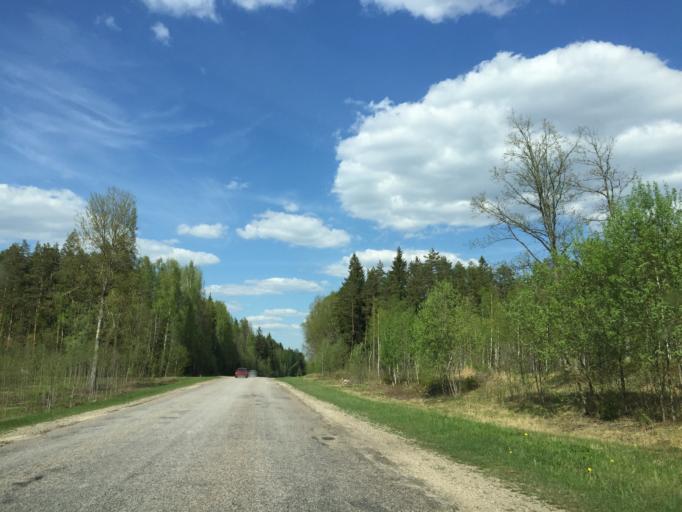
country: LV
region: Limbazu Rajons
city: Limbazi
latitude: 57.4141
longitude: 24.6972
